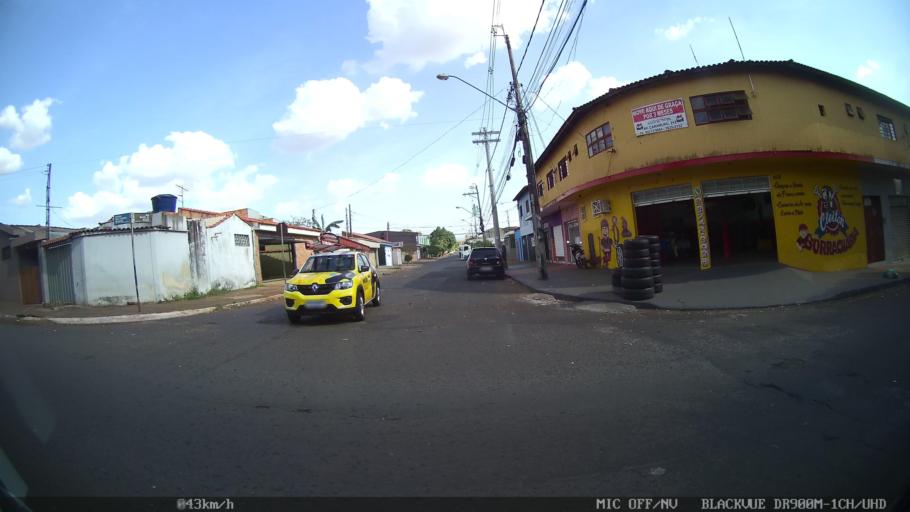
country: BR
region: Sao Paulo
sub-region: Ribeirao Preto
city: Ribeirao Preto
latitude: -21.1991
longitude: -47.8469
